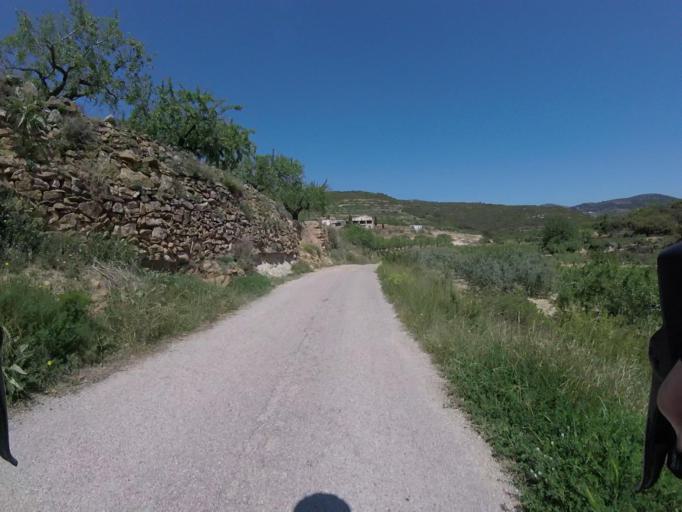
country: ES
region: Valencia
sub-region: Provincia de Castello
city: Sierra-Engarceran
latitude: 40.2481
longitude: -0.0296
